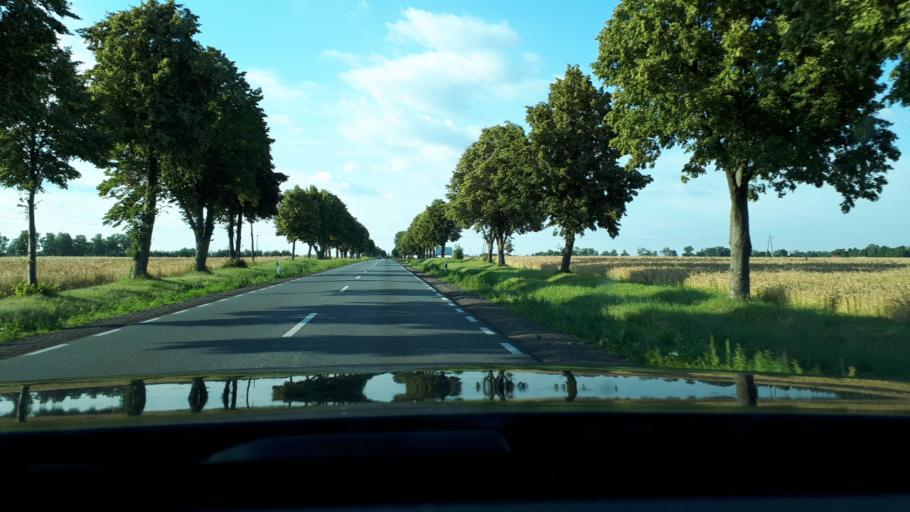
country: PL
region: Masovian Voivodeship
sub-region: Powiat ciechanowski
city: Ciechanow
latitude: 52.8366
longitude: 20.6197
